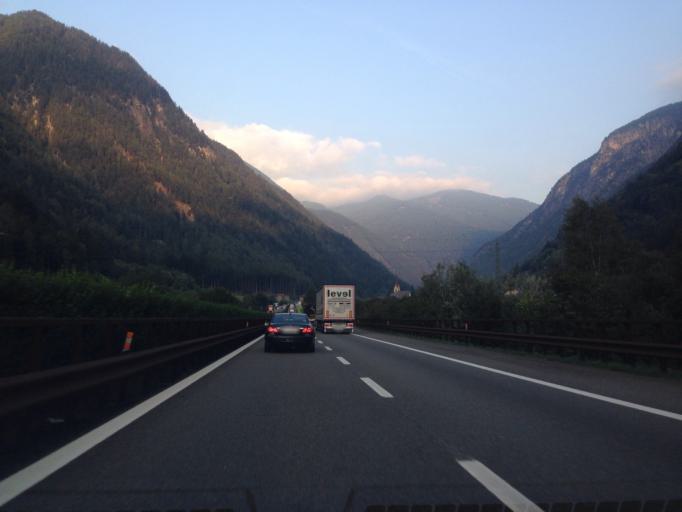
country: IT
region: Trentino-Alto Adige
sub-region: Bolzano
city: Fortezza
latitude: 46.8049
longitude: 11.5832
